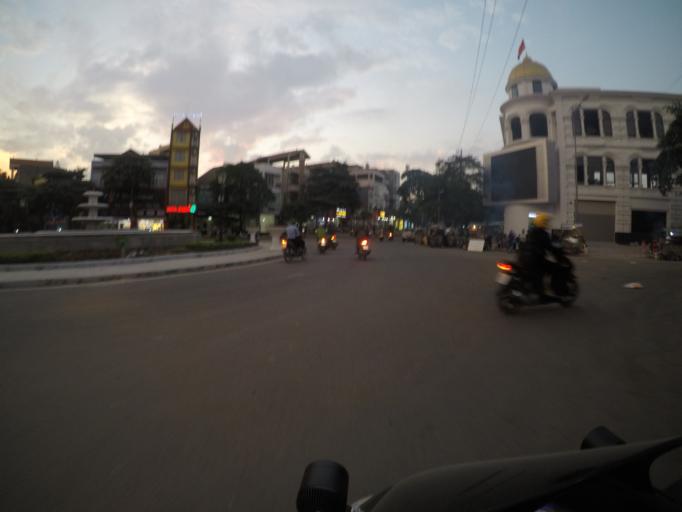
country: VN
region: Vinh Phuc
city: Phuc Yen
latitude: 21.2779
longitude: 105.7295
